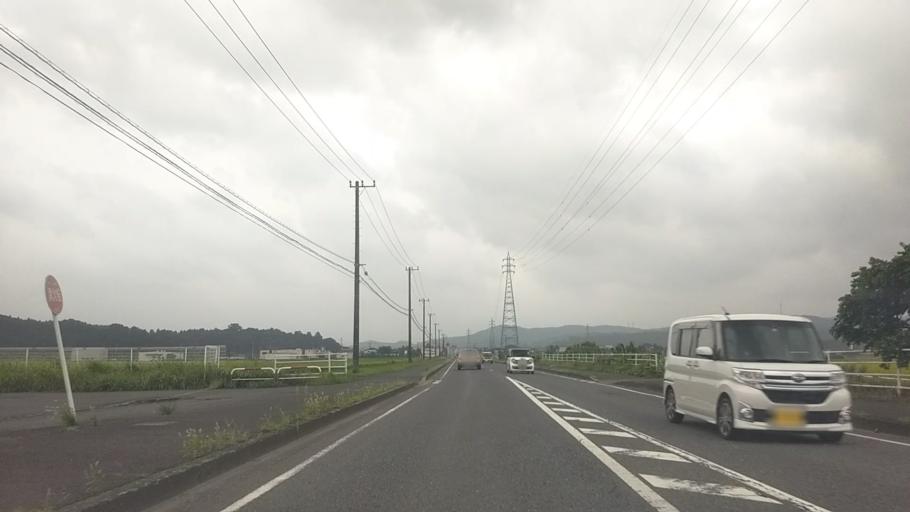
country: JP
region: Chiba
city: Kisarazu
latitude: 35.3296
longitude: 140.0550
